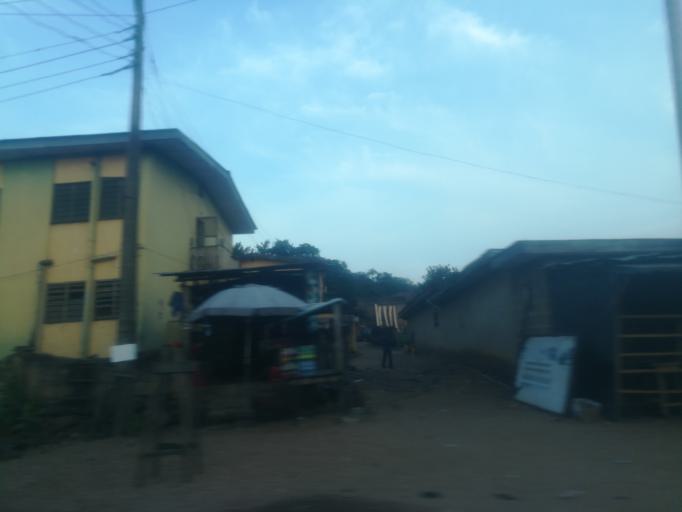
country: NG
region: Ogun
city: Abeokuta
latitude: 7.1433
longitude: 3.3381
